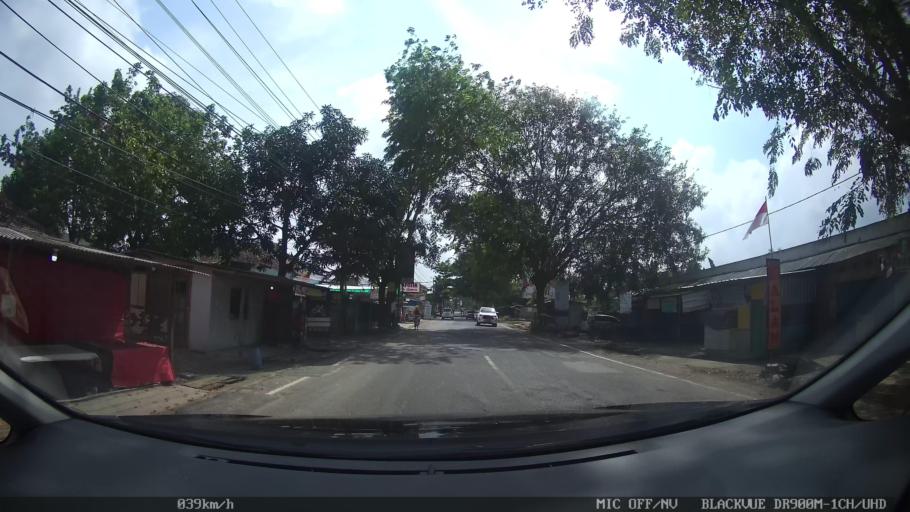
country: ID
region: Lampung
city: Kedaton
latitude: -5.3597
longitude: 105.2838
